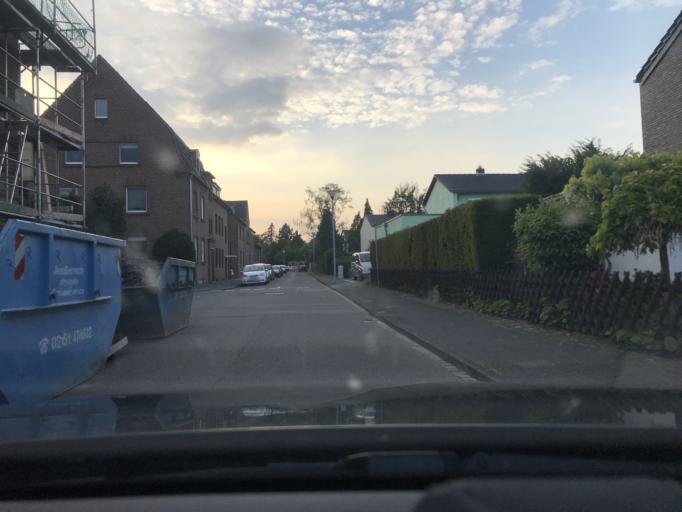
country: DE
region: North Rhine-Westphalia
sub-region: Regierungsbezirk Dusseldorf
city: Krefeld
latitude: 51.3525
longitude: 6.6062
